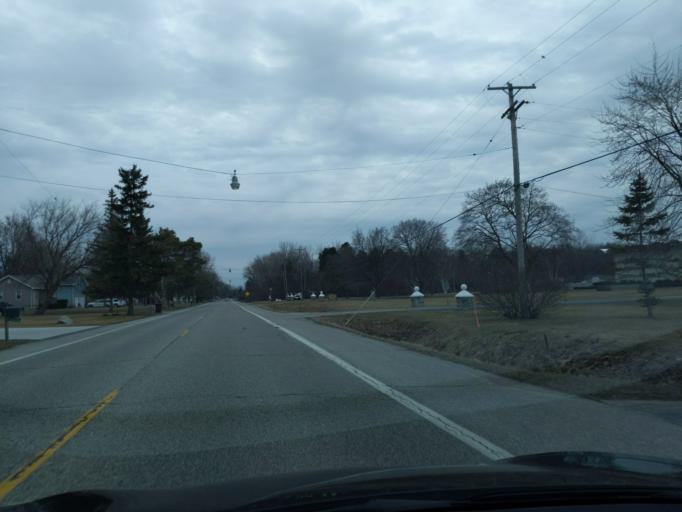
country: US
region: Michigan
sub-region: Bay County
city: Bay City
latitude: 43.6583
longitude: -83.9125
